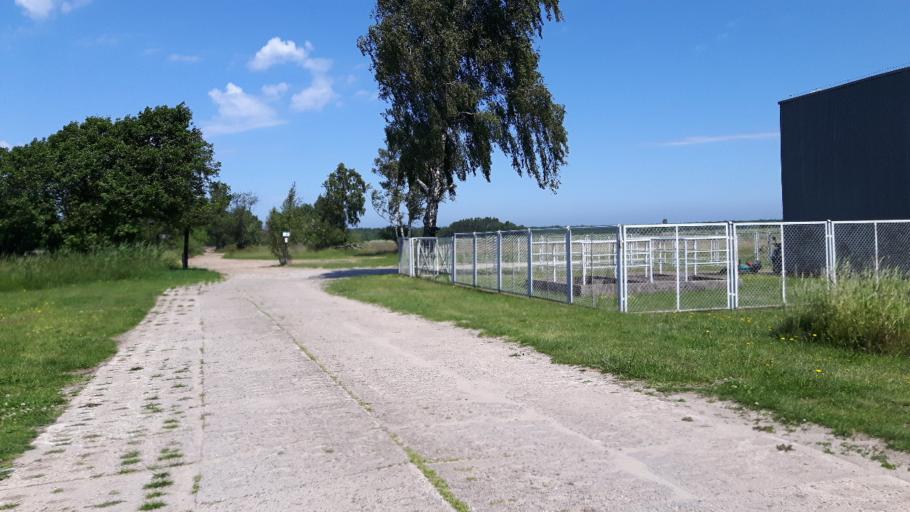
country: PL
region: Pomeranian Voivodeship
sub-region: Powiat slupski
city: Smoldzino
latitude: 54.6686
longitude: 17.1607
